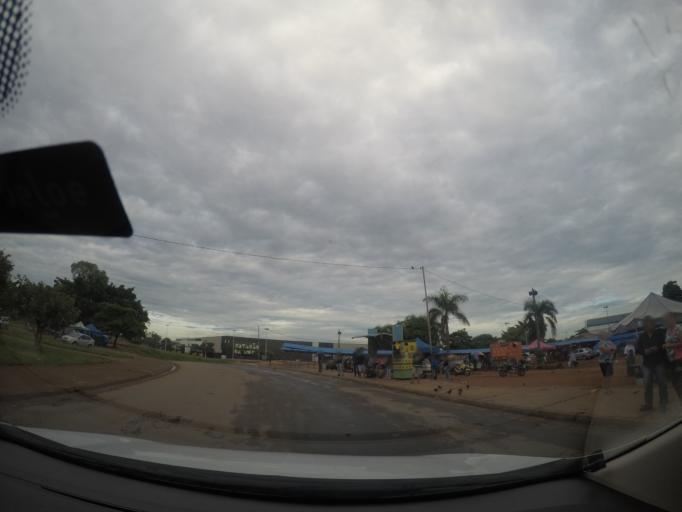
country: BR
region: Goias
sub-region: Goiania
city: Goiania
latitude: -16.6620
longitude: -49.2592
